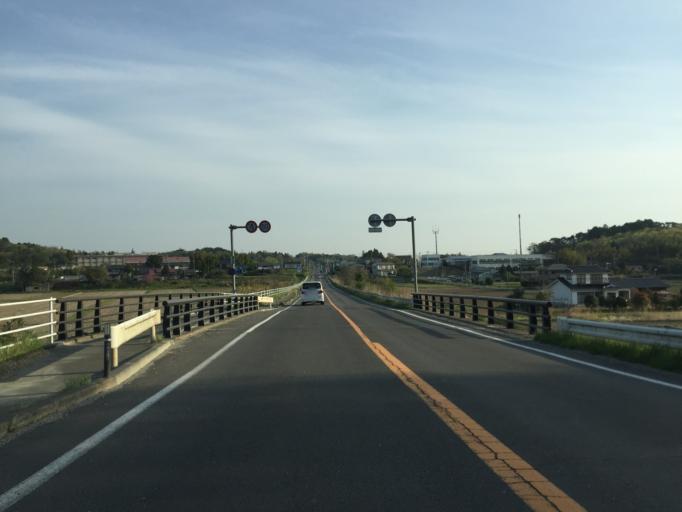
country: JP
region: Miyagi
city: Watari
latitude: 37.9368
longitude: 140.8941
